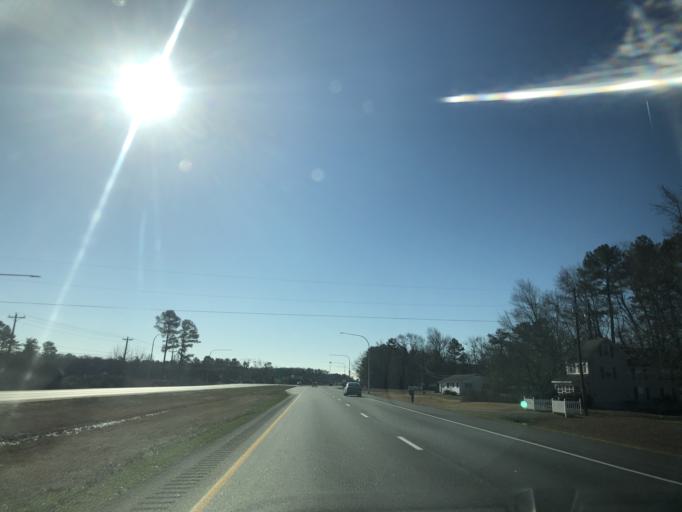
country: US
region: Delaware
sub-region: Sussex County
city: Georgetown
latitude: 38.7187
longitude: -75.4090
